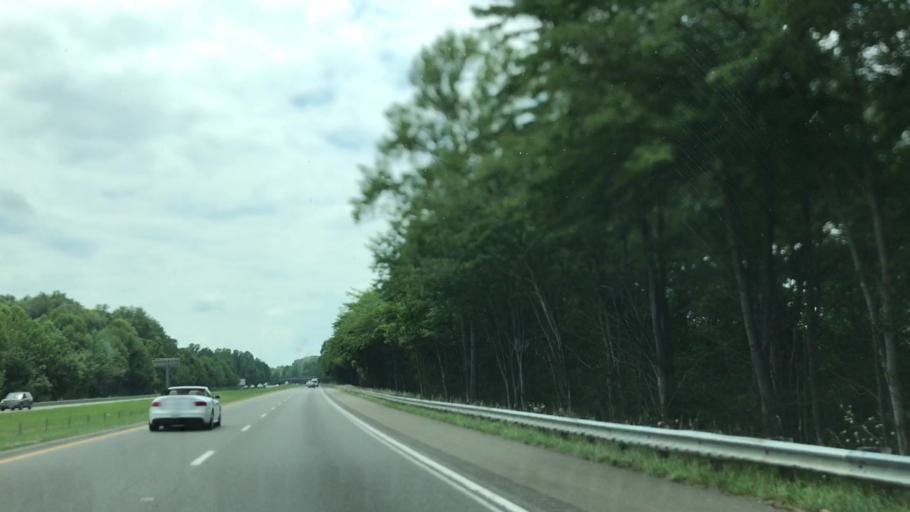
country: US
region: North Carolina
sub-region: Surry County
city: Dobson
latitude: 36.4661
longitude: -80.7596
